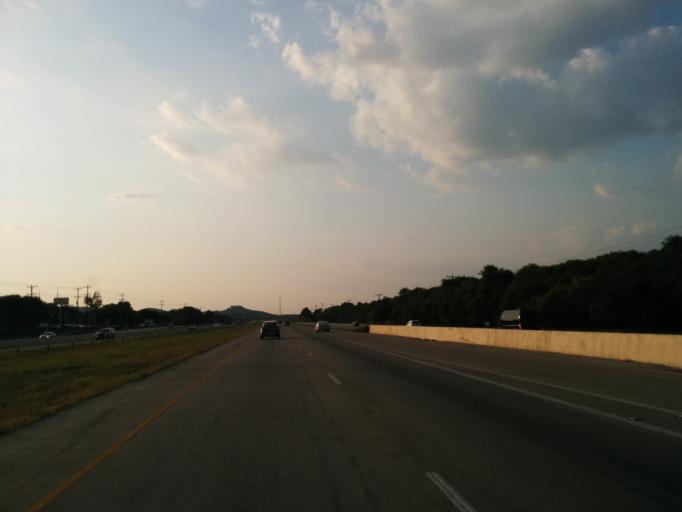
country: US
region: Texas
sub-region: Bexar County
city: Cross Mountain
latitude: 29.6396
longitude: -98.6165
